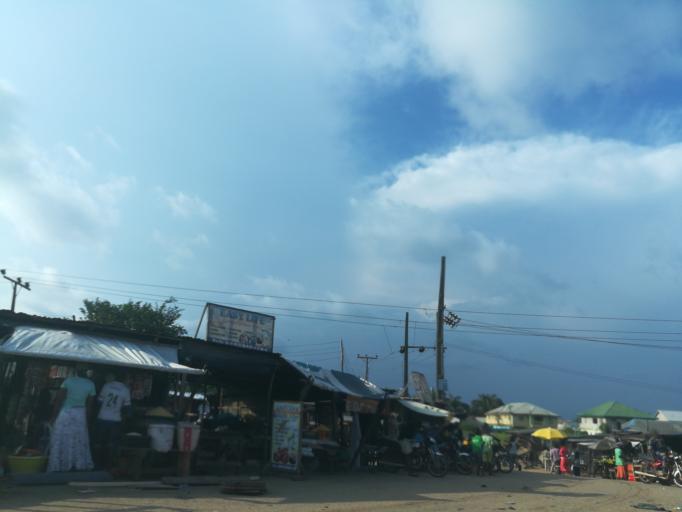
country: NG
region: Ogun
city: Ado Odo
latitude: 6.4861
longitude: 3.0600
